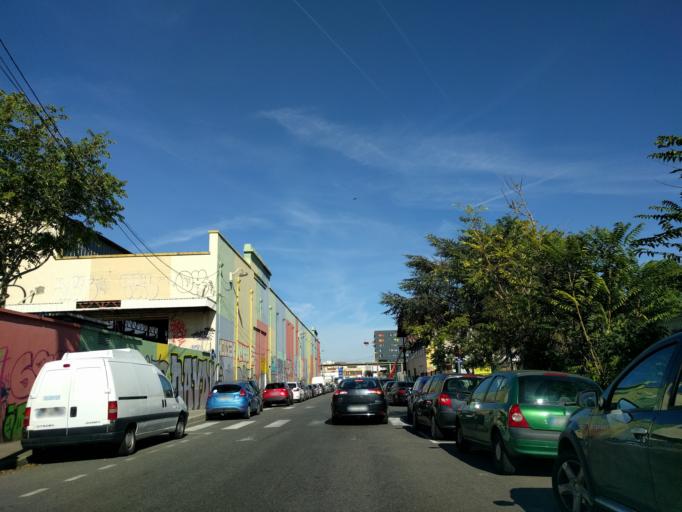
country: FR
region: Rhone-Alpes
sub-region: Departement du Rhone
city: La Mulatiere
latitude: 45.7366
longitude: 4.8187
